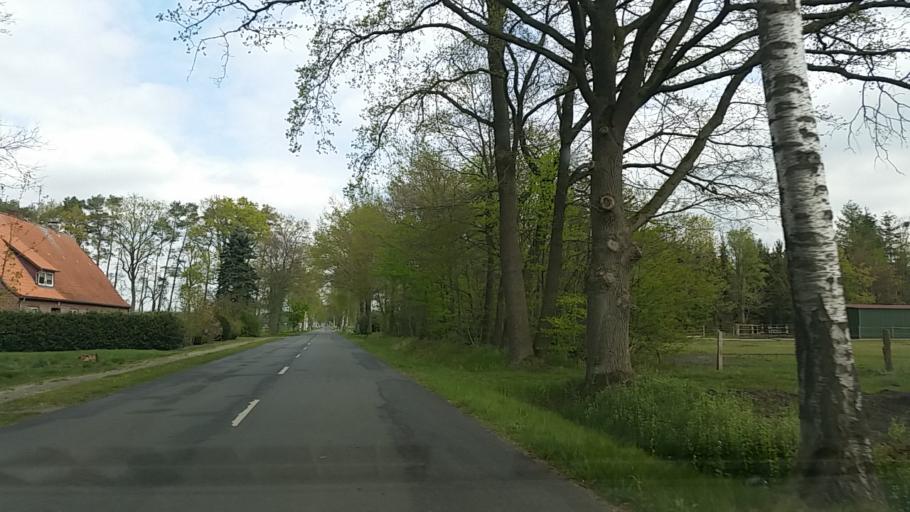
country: DE
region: Lower Saxony
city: Konigsmoor
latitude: 53.2045
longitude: 9.7077
